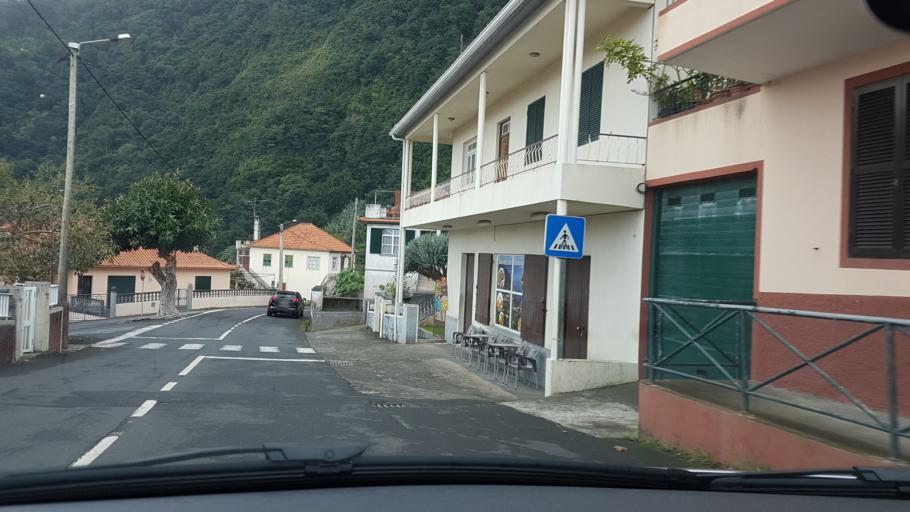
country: PT
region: Madeira
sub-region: Santana
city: Santana
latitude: 32.8248
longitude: -16.9565
